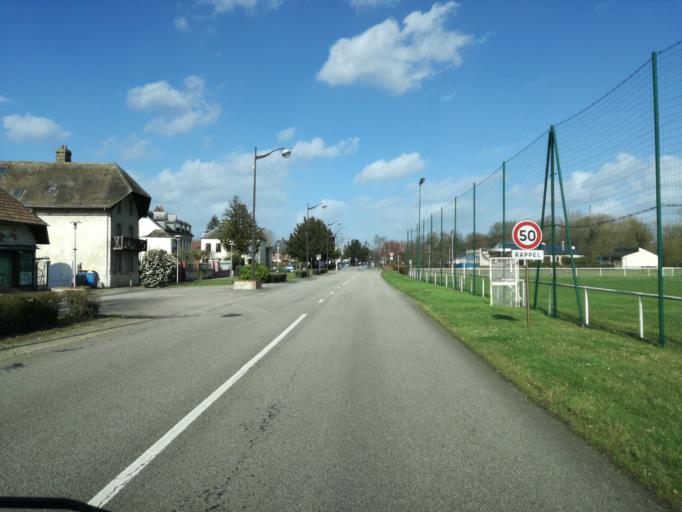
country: FR
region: Haute-Normandie
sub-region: Departement de la Seine-Maritime
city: Petit-Couronne
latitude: 49.3767
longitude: 1.0019
